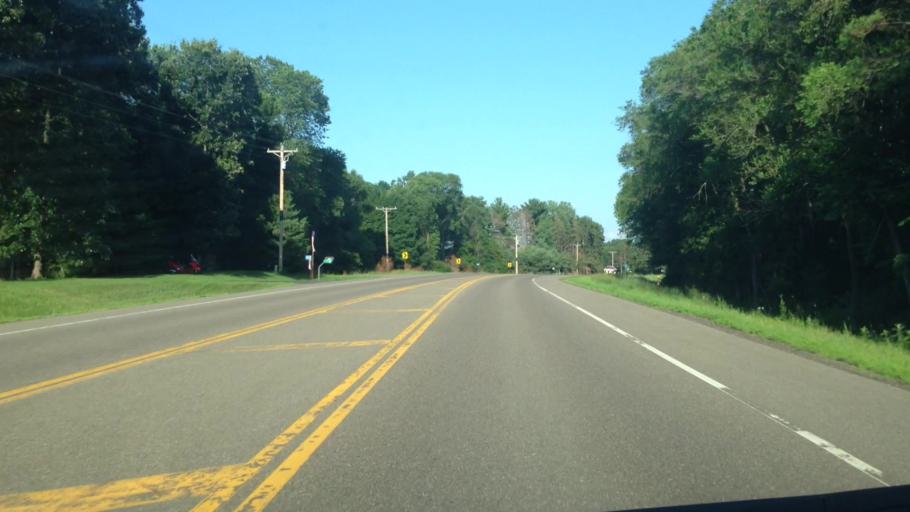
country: US
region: Minnesota
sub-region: Sherburne County
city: Zimmerman
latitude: 45.4446
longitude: -93.6262
